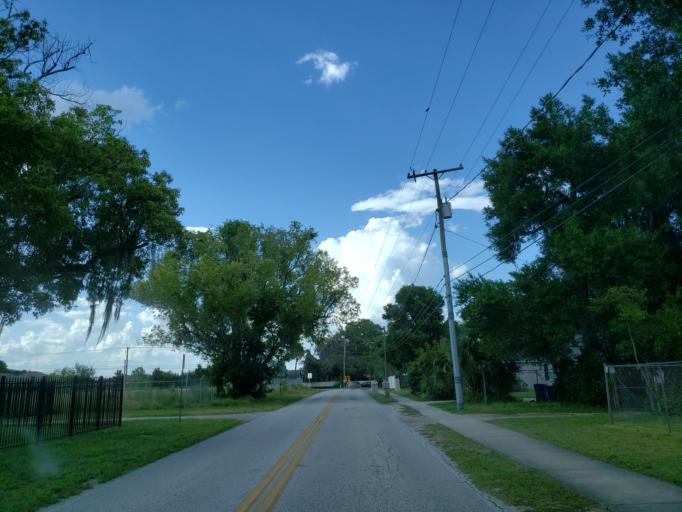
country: US
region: Florida
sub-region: Hillsborough County
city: Mango
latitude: 27.9585
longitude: -82.3022
